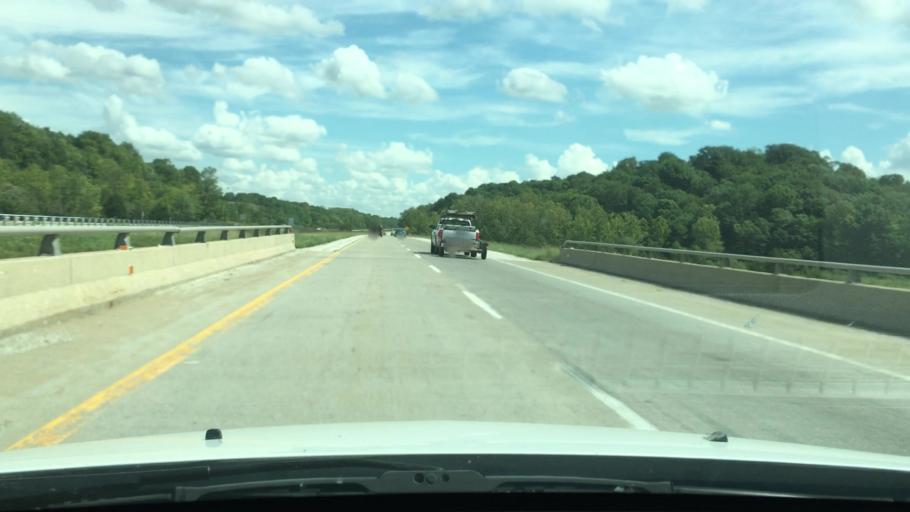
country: US
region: Illinois
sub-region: Scott County
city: Winchester
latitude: 39.6851
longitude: -90.5702
